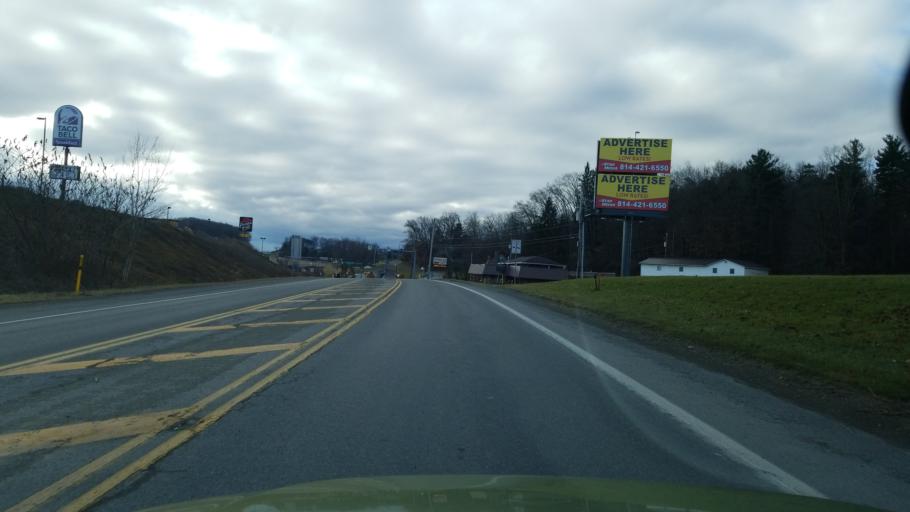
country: US
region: Pennsylvania
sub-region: Jefferson County
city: Punxsutawney
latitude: 40.9296
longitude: -78.9829
